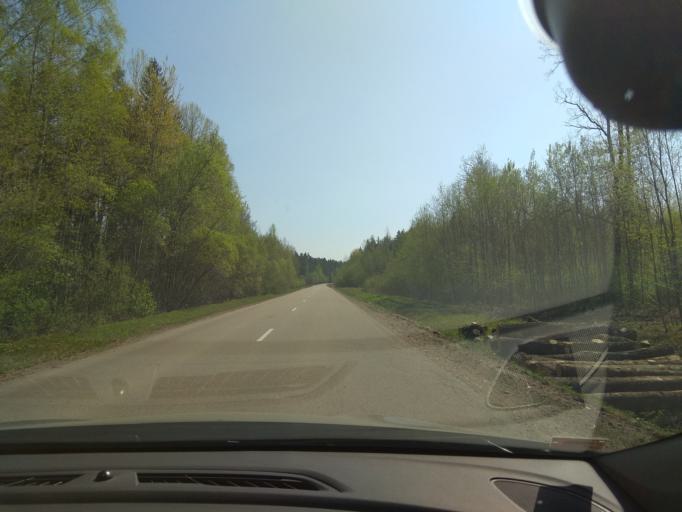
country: LT
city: Linkuva
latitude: 55.9922
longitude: 24.1736
